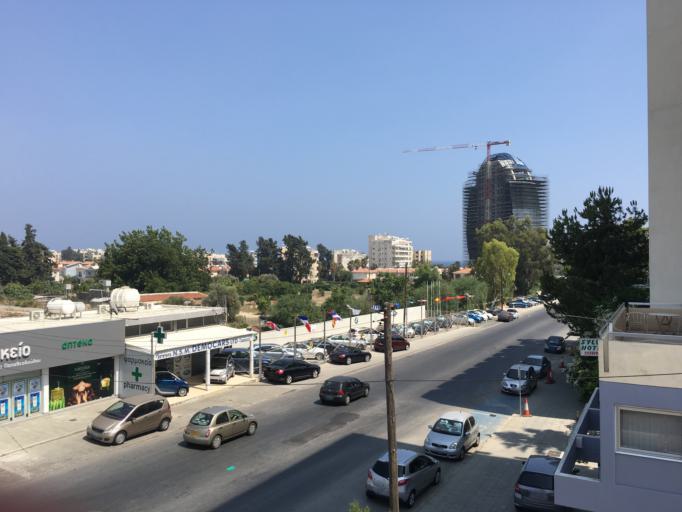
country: CY
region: Limassol
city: Limassol
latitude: 34.6923
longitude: 33.0678
